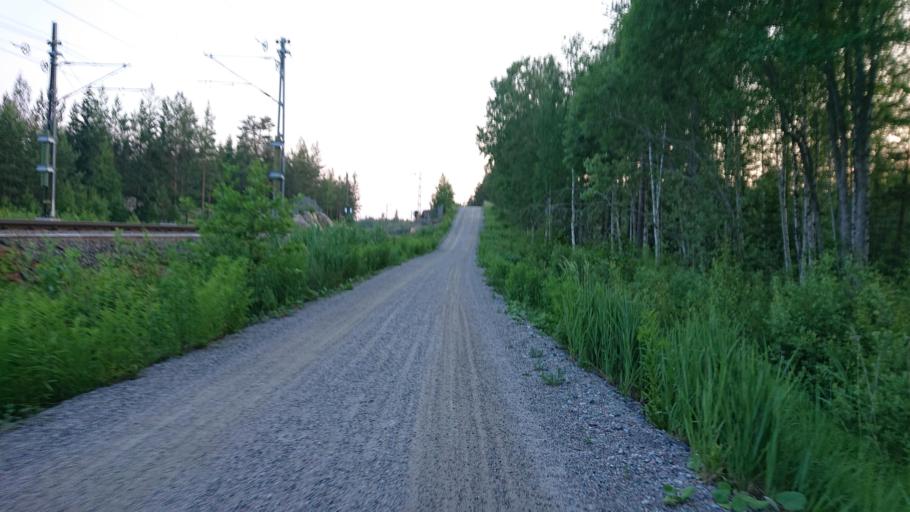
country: SE
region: Stockholm
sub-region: Osterakers Kommun
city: Akersberga
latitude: 59.4691
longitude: 18.2045
